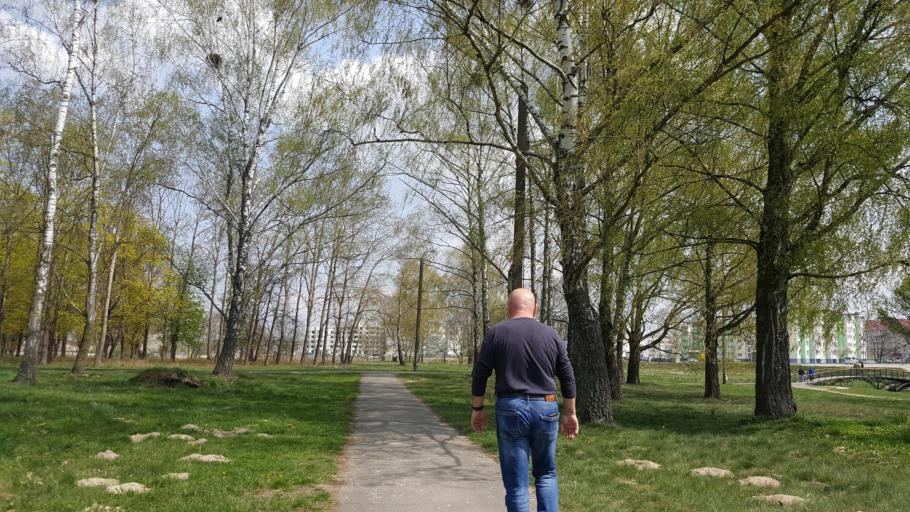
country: BY
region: Brest
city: Zhabinka
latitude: 52.1944
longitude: 24.0277
